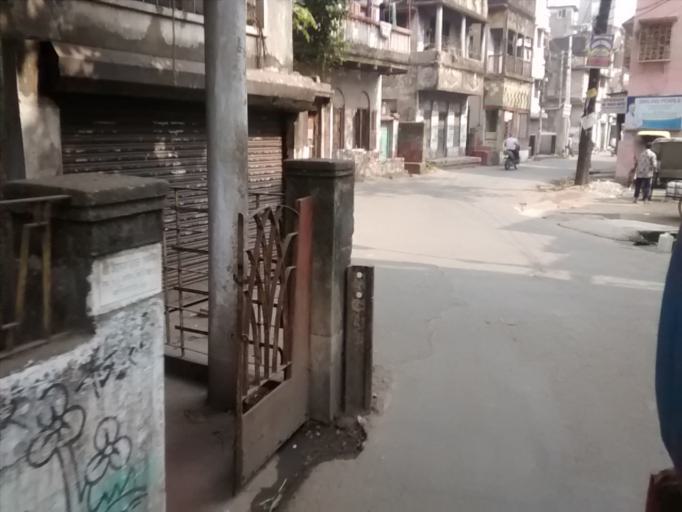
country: IN
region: West Bengal
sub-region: North 24 Parganas
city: Garui
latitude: 22.6245
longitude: 88.3880
